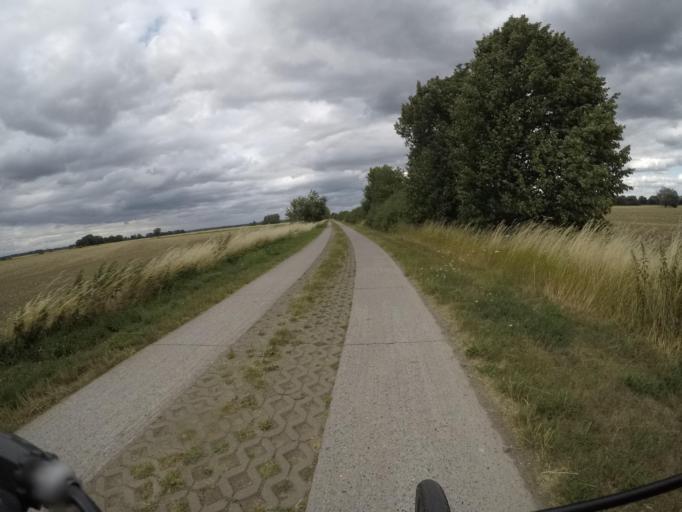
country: DE
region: Lower Saxony
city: Neu Darchau
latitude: 53.2361
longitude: 10.9250
